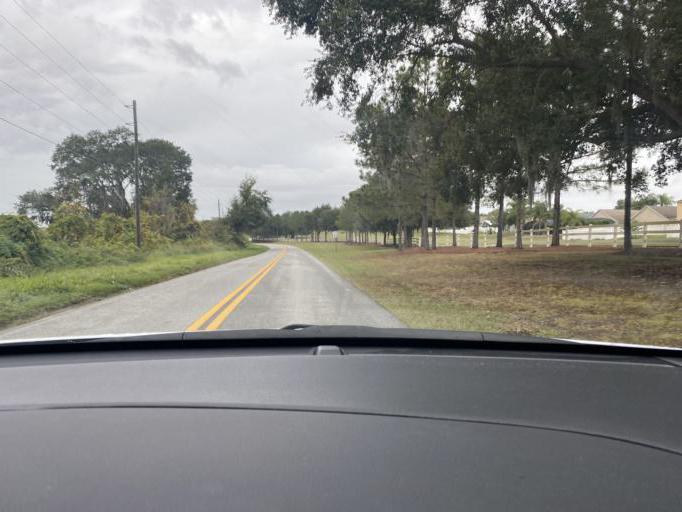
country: US
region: Florida
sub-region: Lake County
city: Minneola
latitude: 28.5964
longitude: -81.7914
